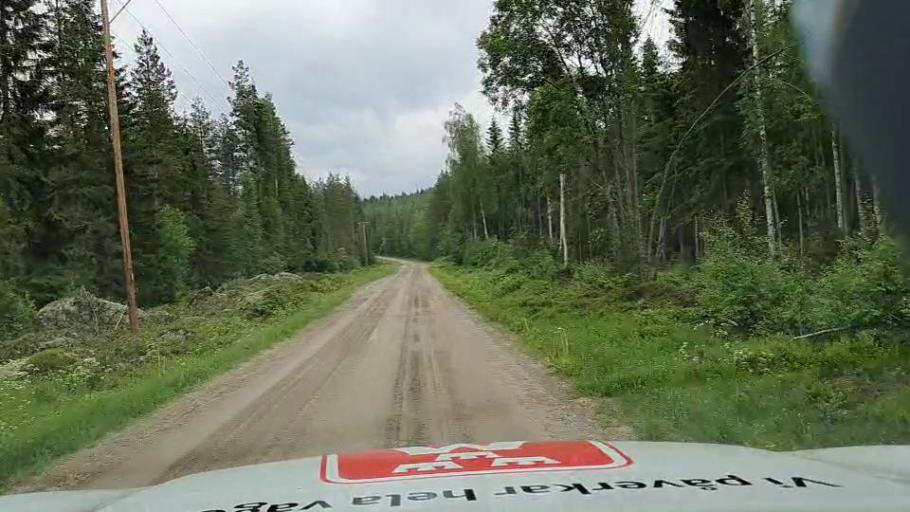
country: SE
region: Vaesternorrland
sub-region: Ange Kommun
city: Fransta
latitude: 62.7768
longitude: 16.1568
